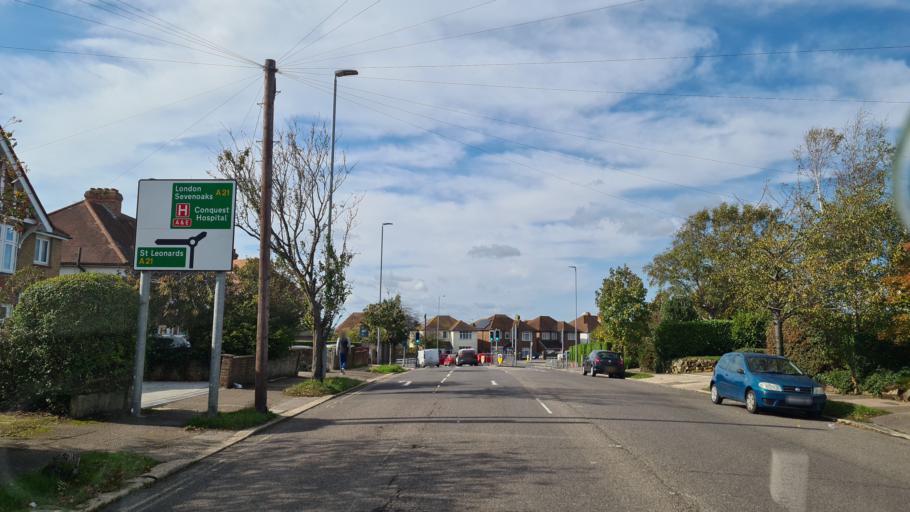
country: GB
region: England
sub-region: East Sussex
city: Hastings
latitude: 50.8755
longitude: 0.5599
